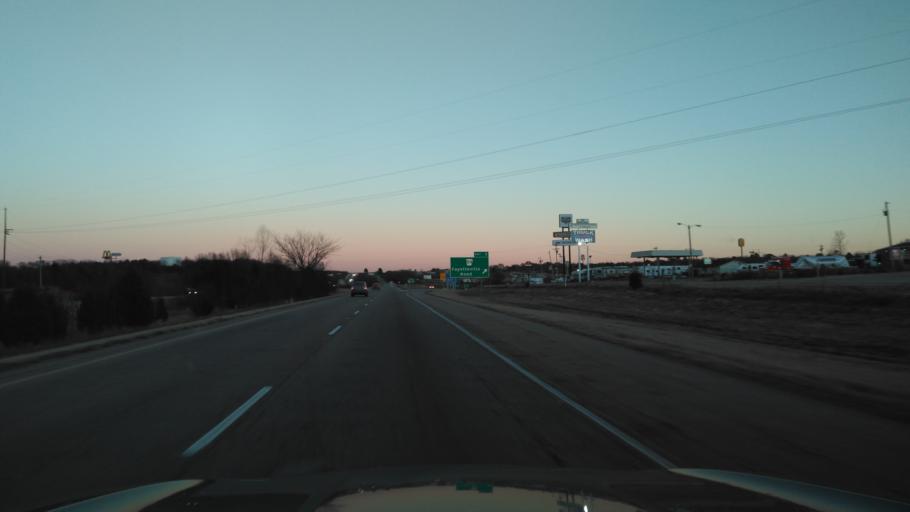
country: US
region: Arkansas
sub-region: Crawford County
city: Van Buren
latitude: 35.4633
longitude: -94.3621
